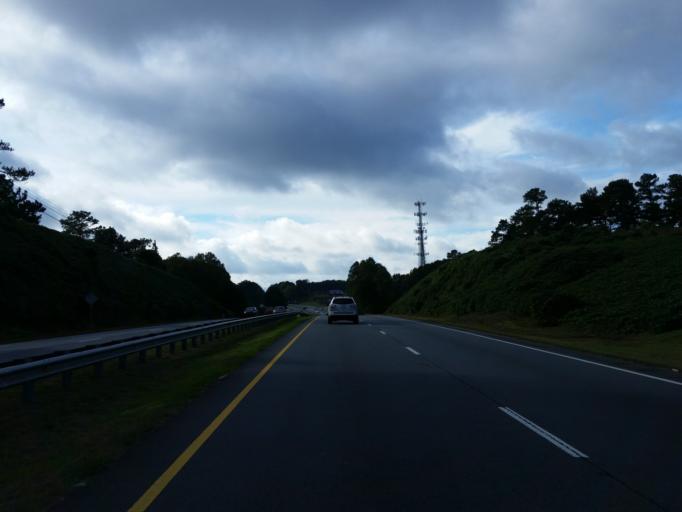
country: US
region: Georgia
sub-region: Cobb County
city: Kennesaw
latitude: 34.0247
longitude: -84.6315
